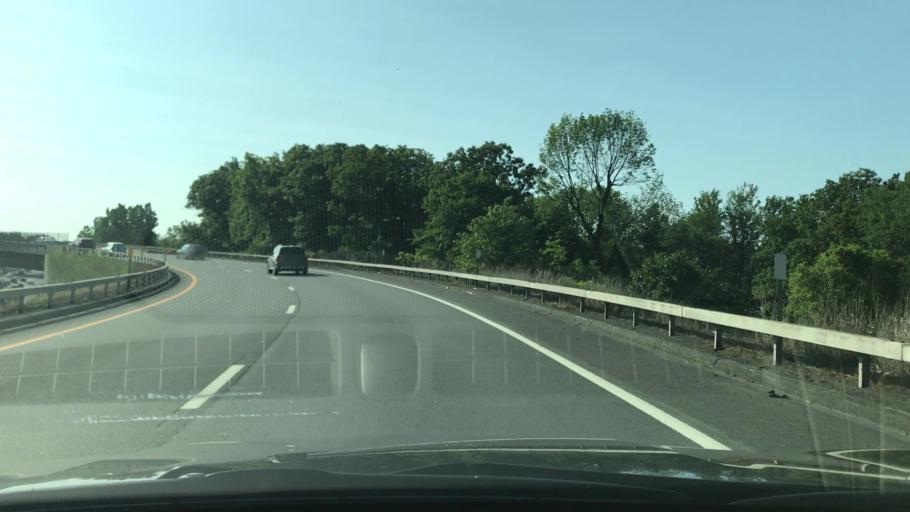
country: US
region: New York
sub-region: Albany County
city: McKownville
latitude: 42.7018
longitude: -73.8457
